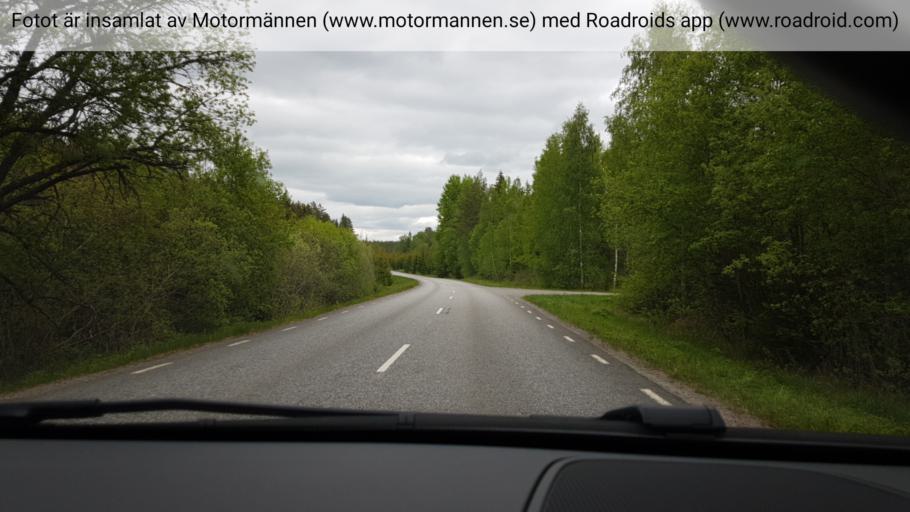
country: SE
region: Uppsala
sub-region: Heby Kommun
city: OEstervala
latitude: 60.0906
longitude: 17.0892
